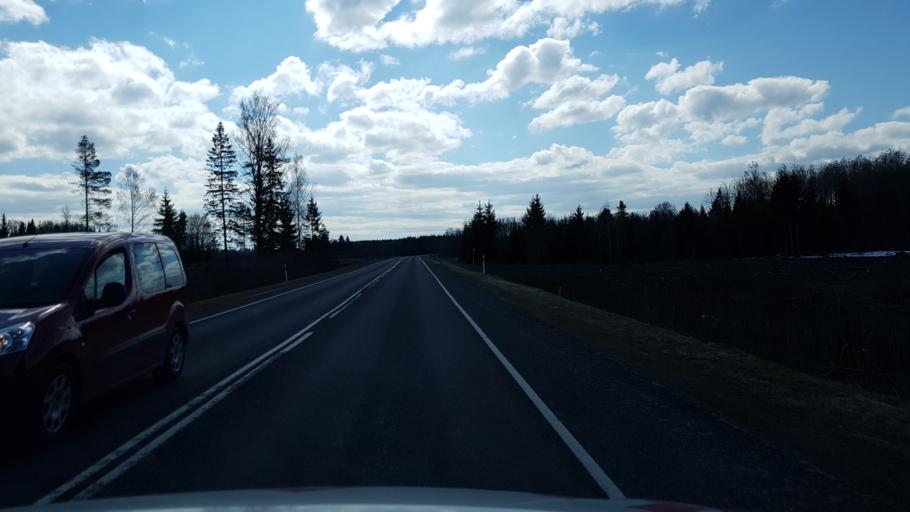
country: EE
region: Laeaene-Virumaa
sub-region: Rakvere linn
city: Rakvere
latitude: 59.2651
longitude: 26.2845
